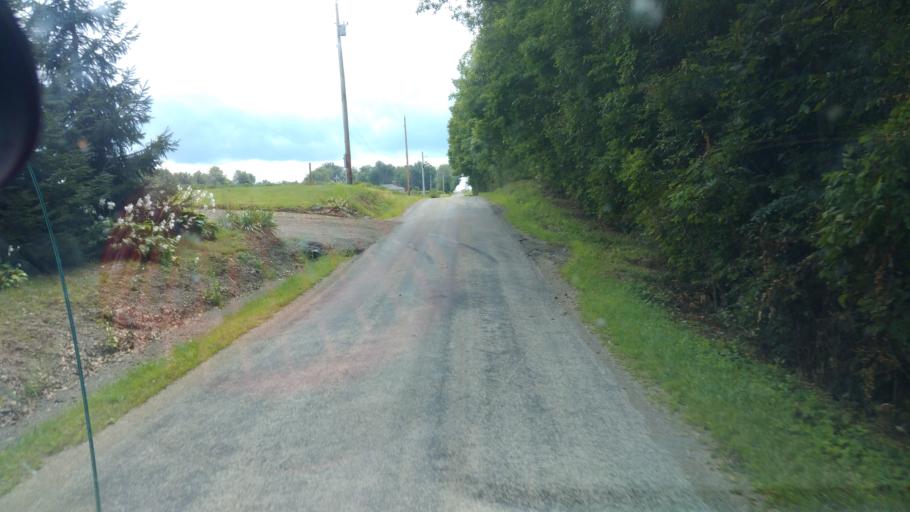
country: US
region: Ohio
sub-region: Ashland County
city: Ashland
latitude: 40.7989
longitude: -82.3691
